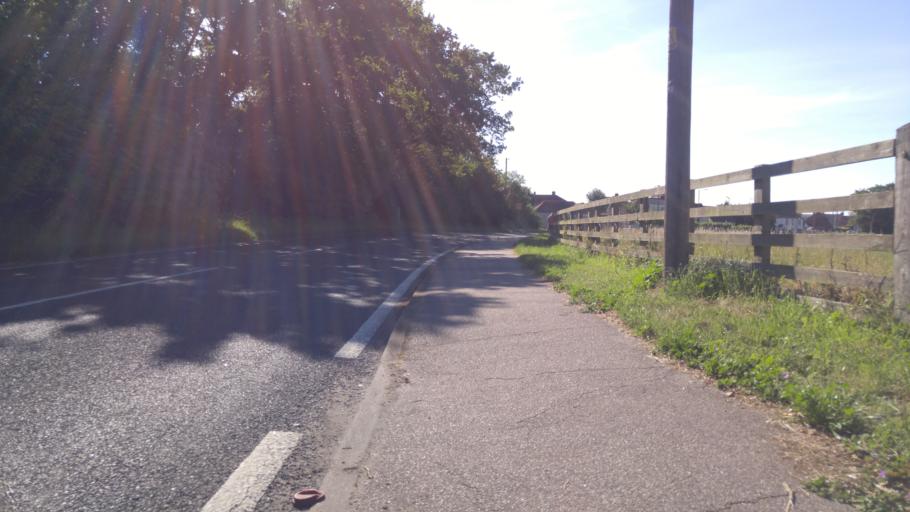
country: GB
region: England
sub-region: Essex
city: Rowhedge
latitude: 51.8639
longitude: 0.9342
